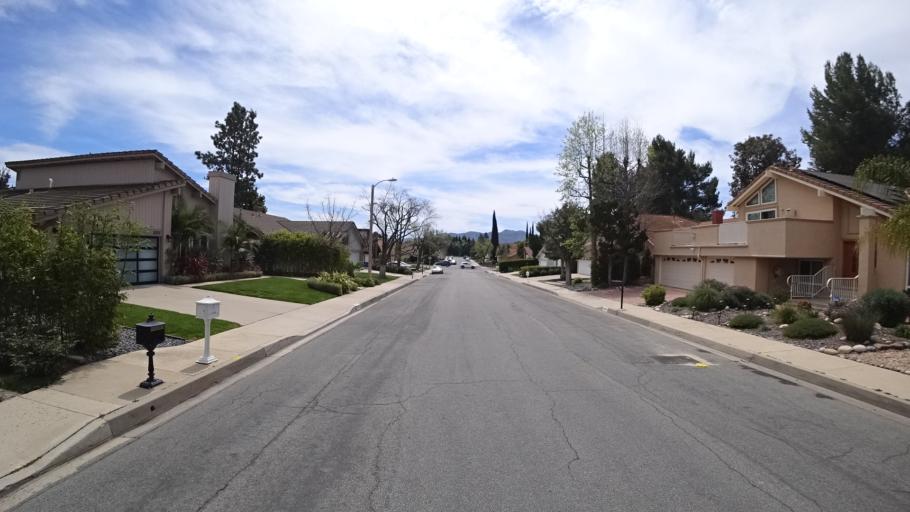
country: US
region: California
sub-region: Ventura County
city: Thousand Oaks
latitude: 34.1696
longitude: -118.8320
